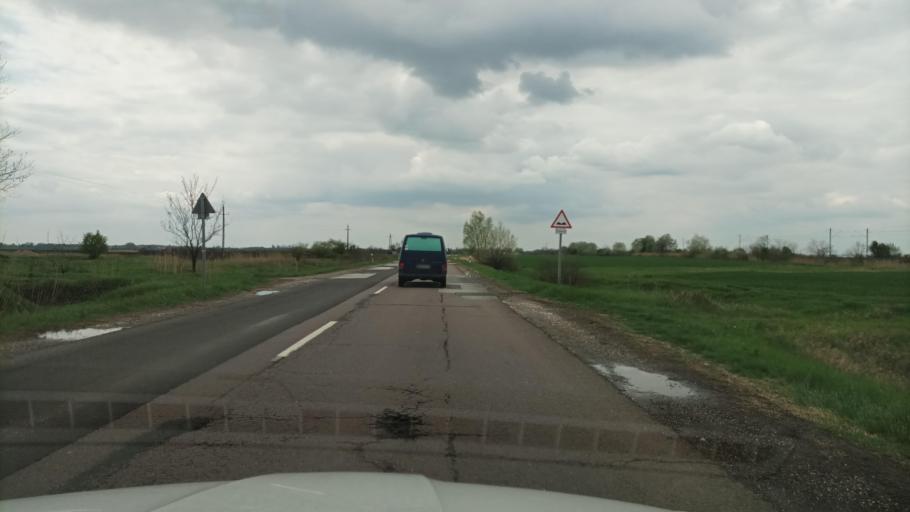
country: HU
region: Pest
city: Cegled
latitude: 47.1799
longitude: 19.8701
